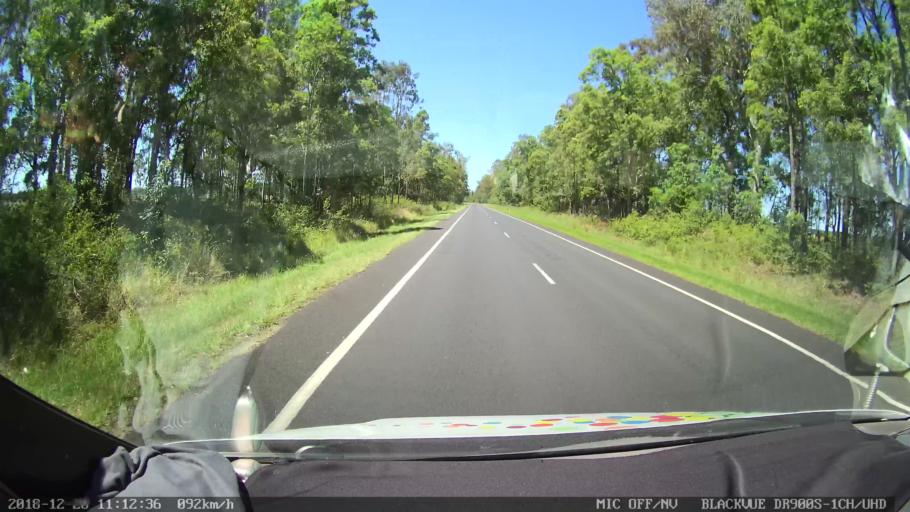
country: AU
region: New South Wales
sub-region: Richmond Valley
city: Casino
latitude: -28.9762
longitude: 153.0105
